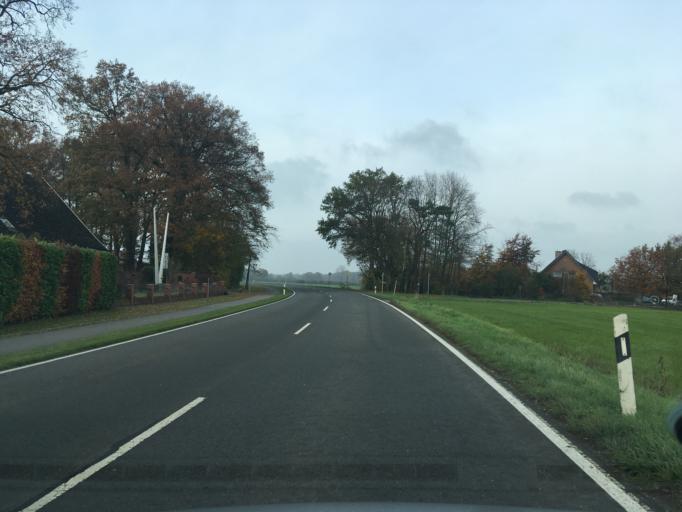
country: DE
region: North Rhine-Westphalia
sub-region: Regierungsbezirk Munster
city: Sudlohn
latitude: 51.9533
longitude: 6.8550
